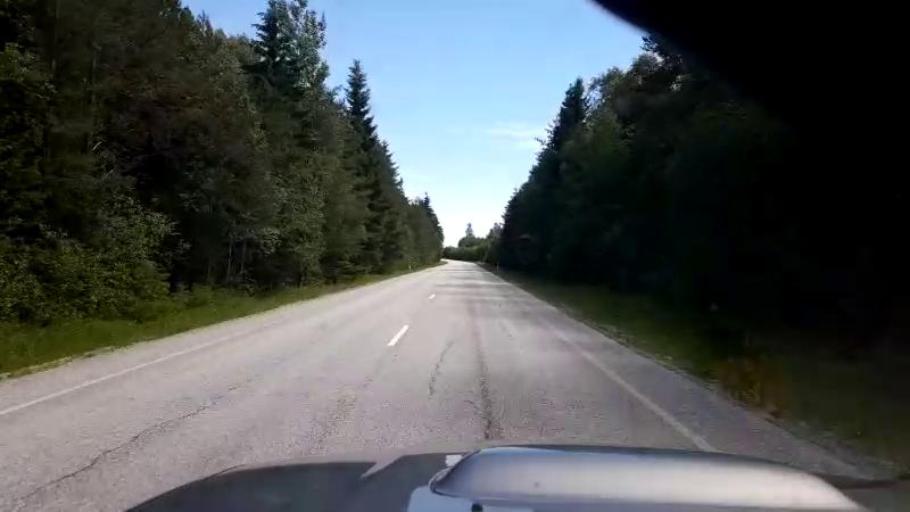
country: EE
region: Laeaene-Virumaa
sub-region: Rakke vald
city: Rakke
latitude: 58.9220
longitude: 26.2434
